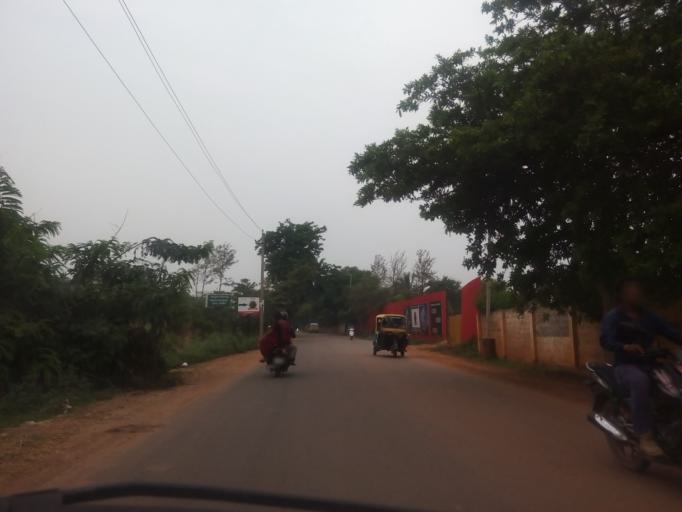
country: IN
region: Karnataka
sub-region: Bangalore Urban
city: Anekal
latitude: 12.8379
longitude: 77.6837
